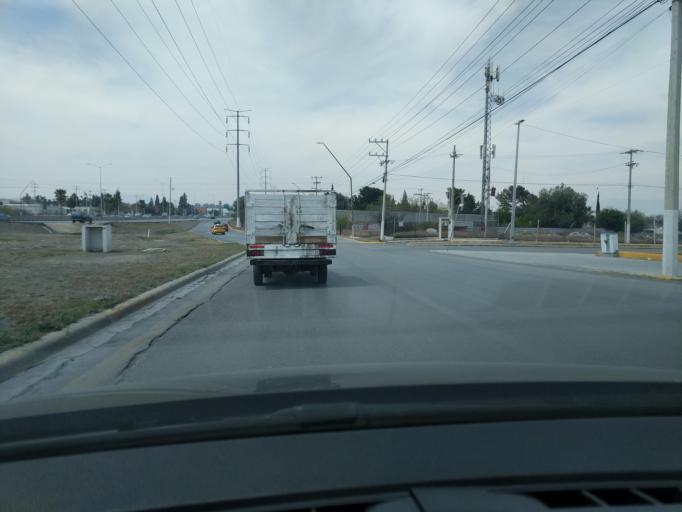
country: MX
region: Coahuila
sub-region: Arteaga
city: Arteaga
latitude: 25.4355
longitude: -100.9158
